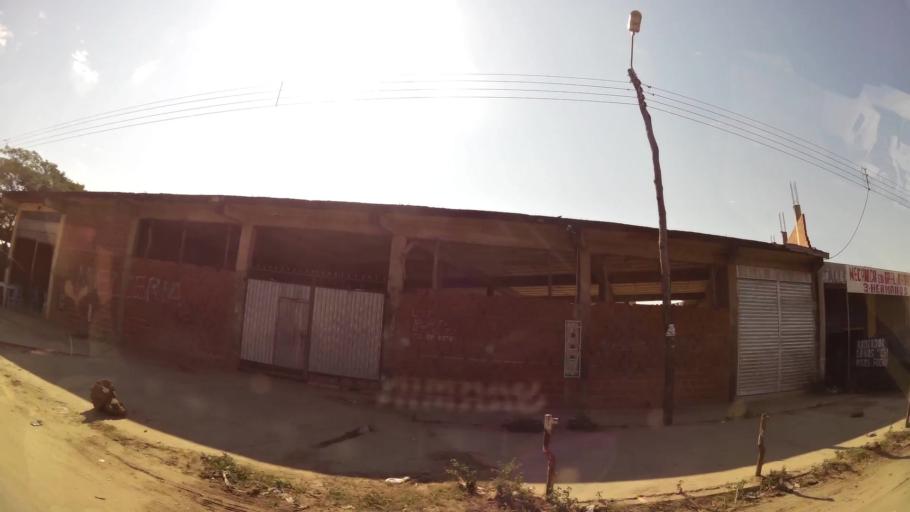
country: BO
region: Santa Cruz
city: Cotoca
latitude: -17.8144
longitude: -63.1112
